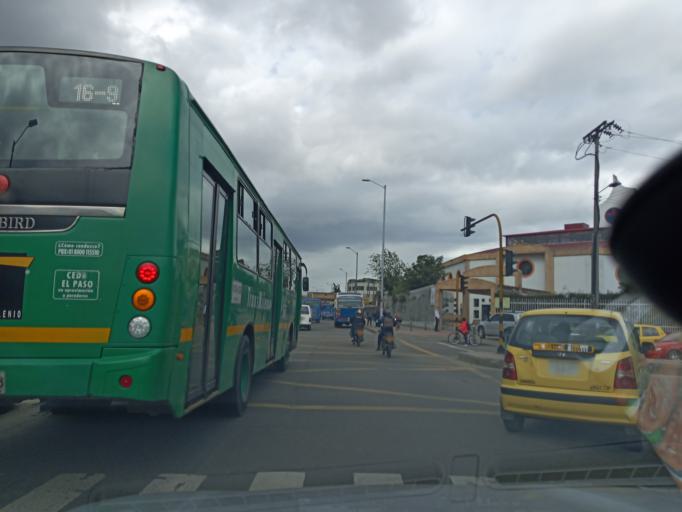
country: CO
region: Cundinamarca
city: Funza
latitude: 4.6813
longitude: -74.1342
